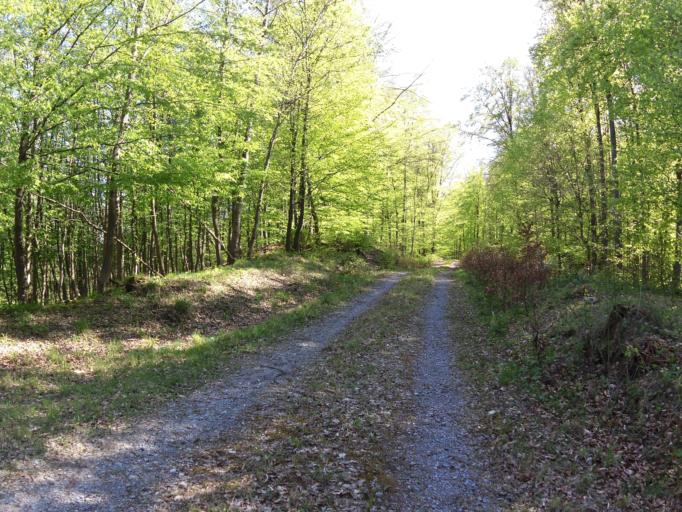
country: DE
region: Thuringia
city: Wolfsburg-Unkeroda
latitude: 50.9700
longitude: 10.2486
